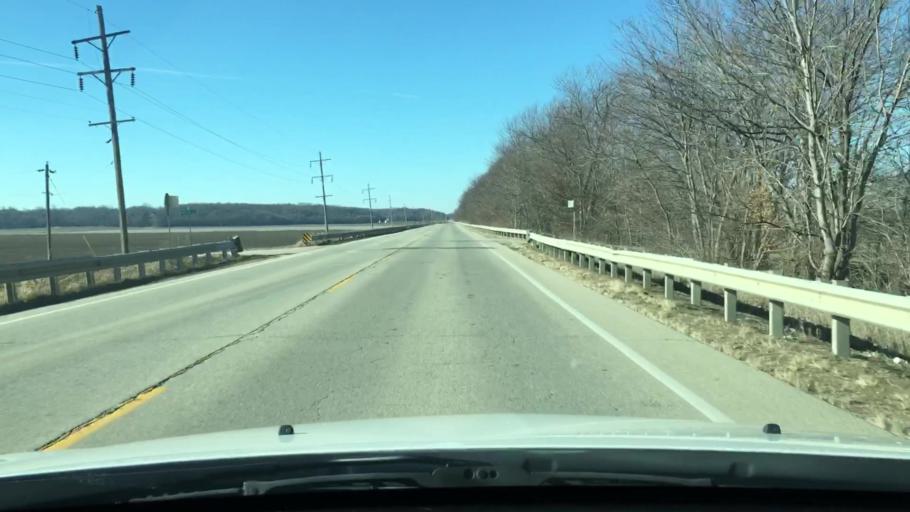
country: US
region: Illinois
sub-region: Mason County
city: Havana
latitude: 40.2998
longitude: -90.1053
